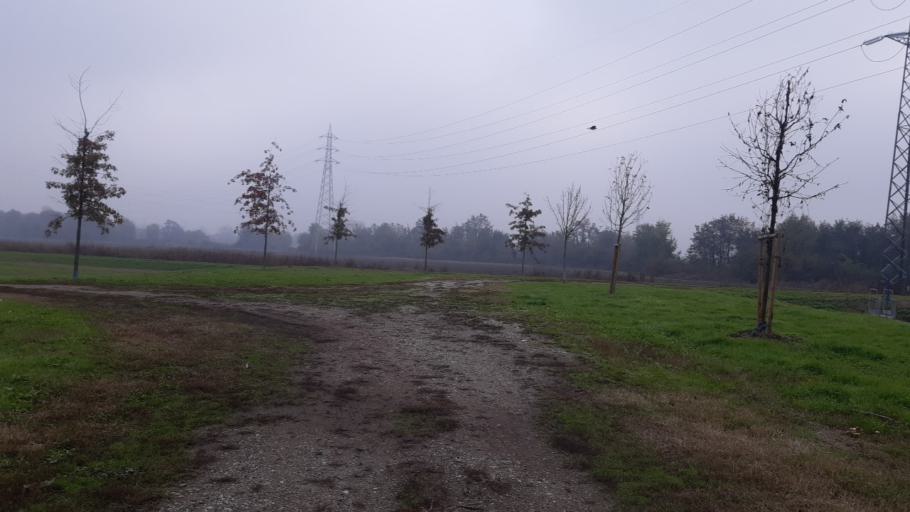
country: IT
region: Lombardy
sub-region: Citta metropolitana di Milano
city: Chiaravalle
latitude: 45.4190
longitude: 9.2264
